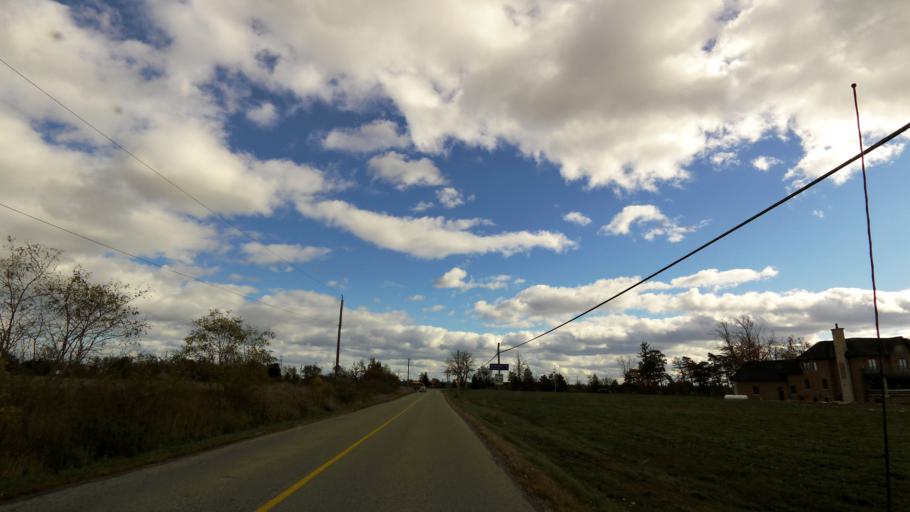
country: CA
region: Ontario
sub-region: Halton
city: Milton
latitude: 43.4877
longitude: -79.7880
